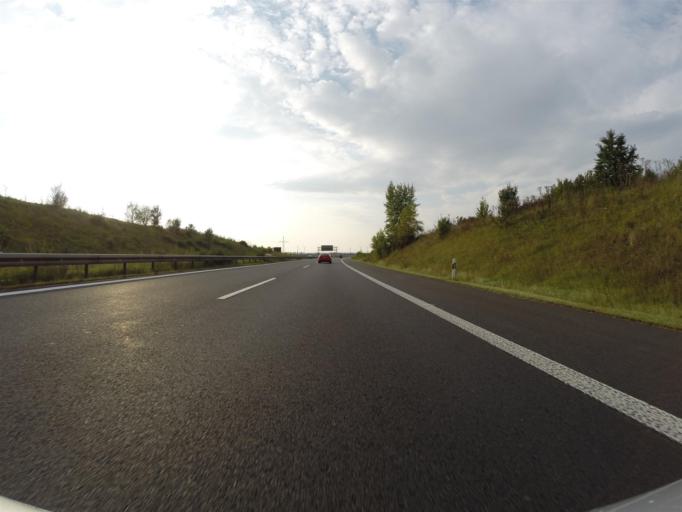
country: DE
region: Saxony-Anhalt
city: Grosskorbetha
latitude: 51.2393
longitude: 12.0347
